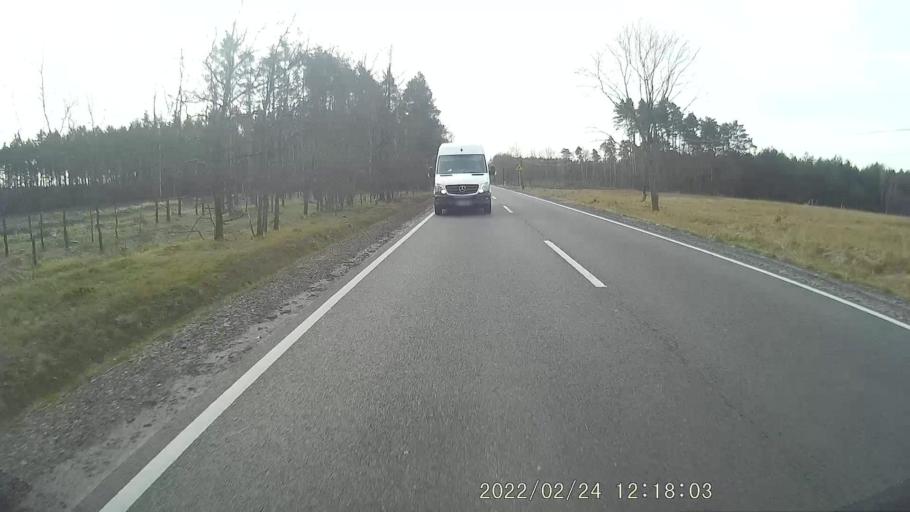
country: PL
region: Lower Silesian Voivodeship
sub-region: Powiat glogowski
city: Glogow
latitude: 51.6495
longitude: 16.0725
